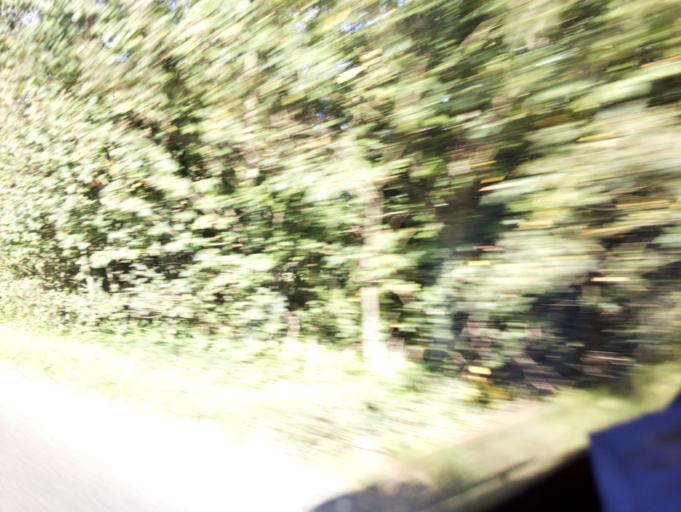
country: GB
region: England
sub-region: Hampshire
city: Alton
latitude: 51.1245
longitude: -0.9925
